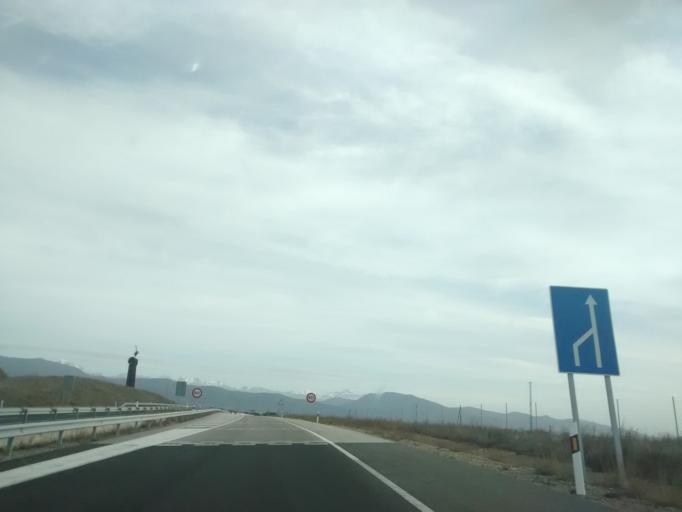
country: ES
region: Aragon
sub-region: Provincia de Zaragoza
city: Mianos
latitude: 42.6112
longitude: -0.9169
